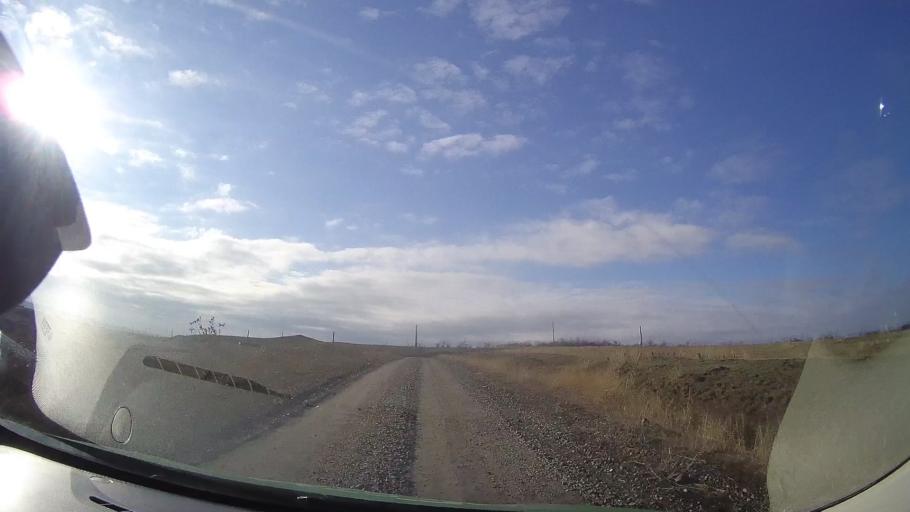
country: RO
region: Mures
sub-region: Comuna Saulia
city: Saulia
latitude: 46.5964
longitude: 24.2209
